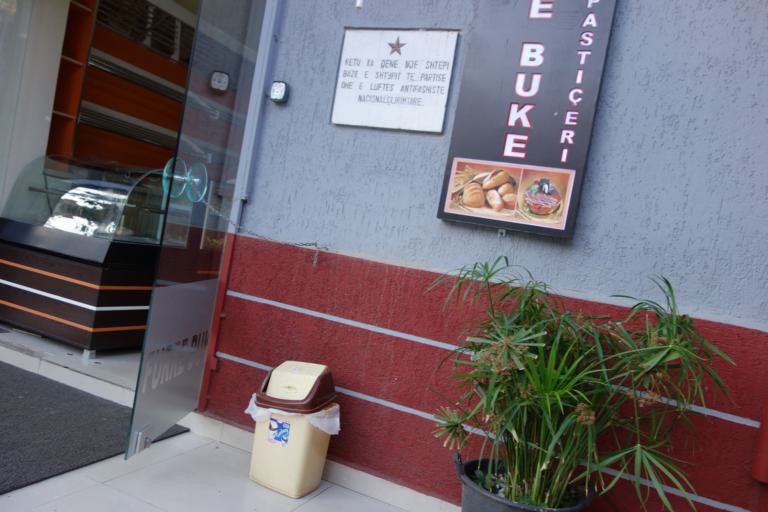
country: AL
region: Tirane
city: Tirana
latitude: 41.3239
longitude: 19.8068
